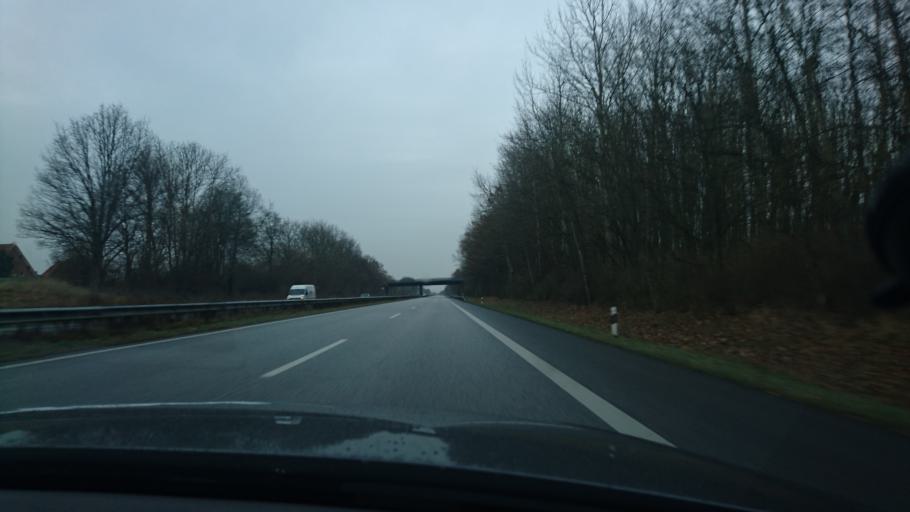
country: DE
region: Schleswig-Holstein
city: Beschendorf
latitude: 54.1607
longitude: 10.8648
